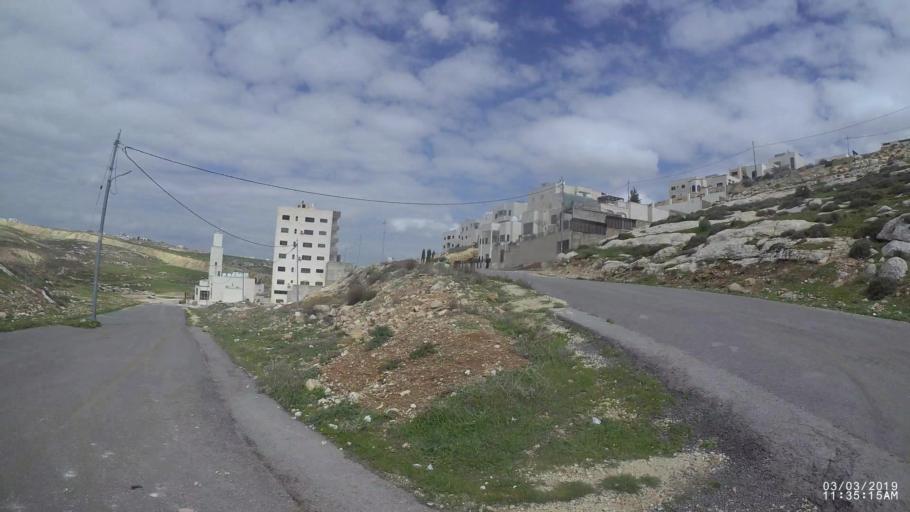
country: JO
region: Amman
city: Al Jubayhah
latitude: 32.0036
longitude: 35.9113
